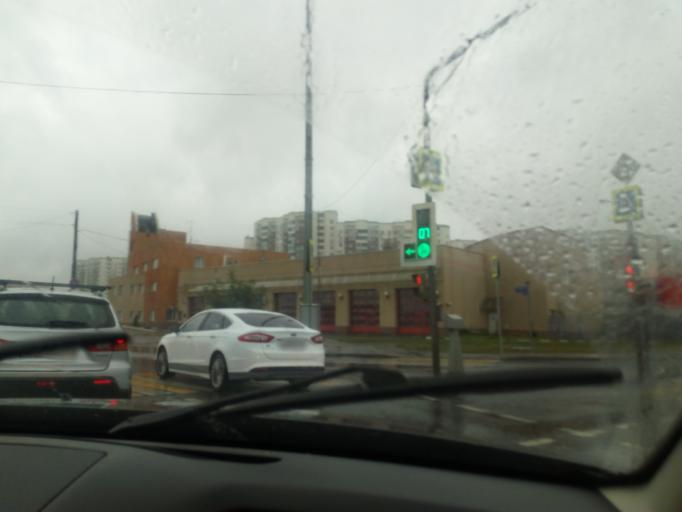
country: RU
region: Moscow
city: Zhulebino
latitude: 55.7091
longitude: 37.8780
